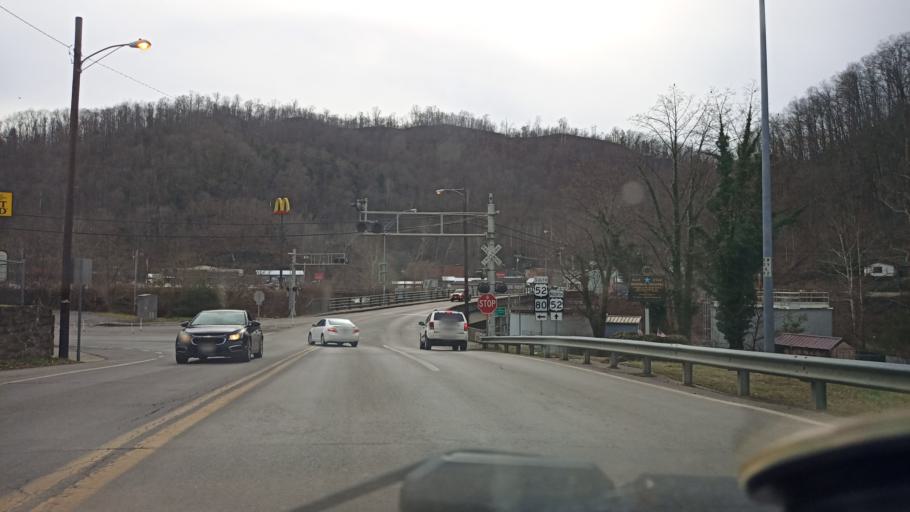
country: US
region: West Virginia
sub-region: Mingo County
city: Gilbert Creek
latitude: 37.6150
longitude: -81.8652
